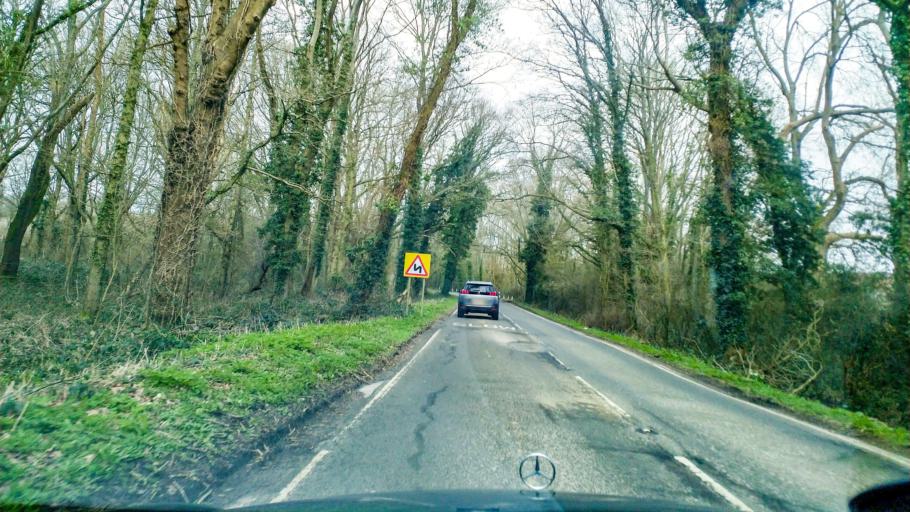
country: GB
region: England
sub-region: Surrey
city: Dorking
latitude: 51.2113
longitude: -0.3119
